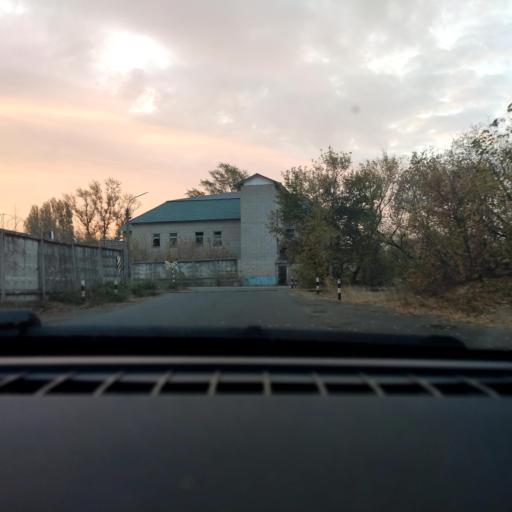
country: RU
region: Voronezj
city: Voronezh
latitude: 51.6478
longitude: 39.2763
